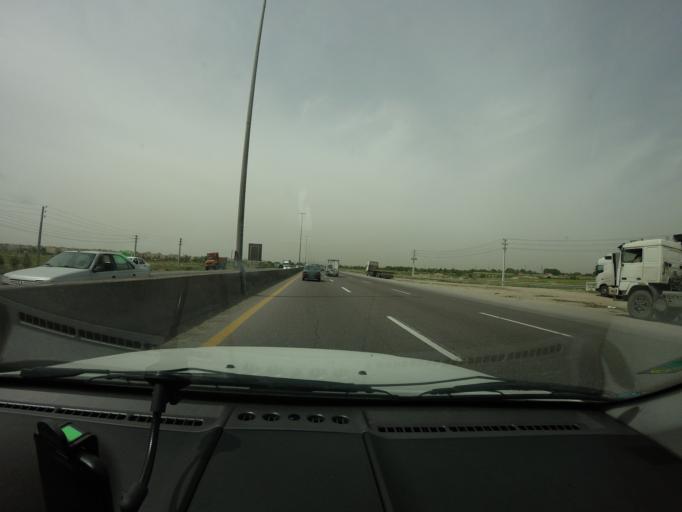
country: IR
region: Tehran
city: Eslamshahr
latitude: 35.5822
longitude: 51.1600
